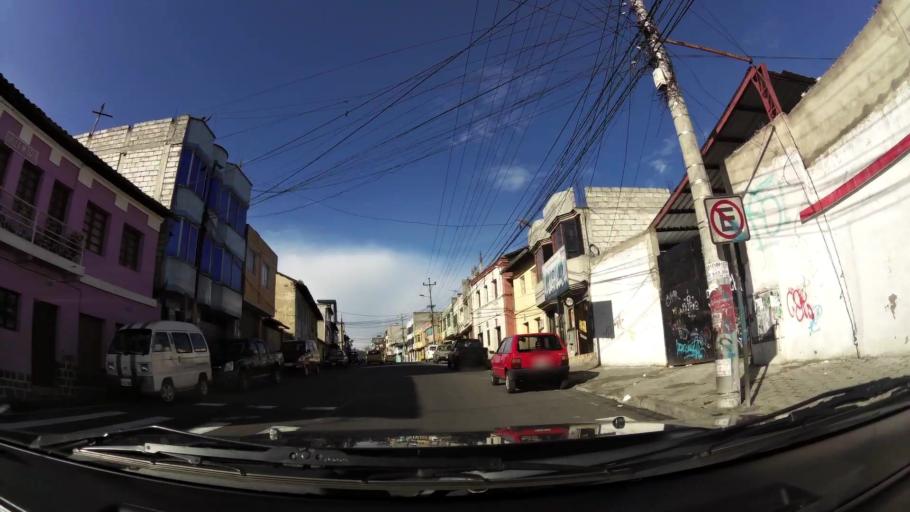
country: EC
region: Pichincha
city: Quito
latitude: -0.2639
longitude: -78.5267
